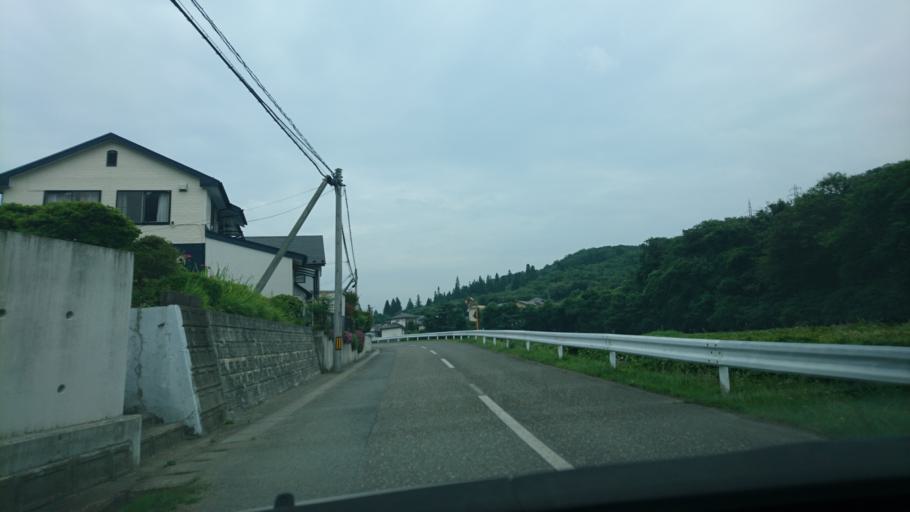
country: JP
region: Iwate
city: Ichinoseki
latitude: 38.9088
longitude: 141.1199
